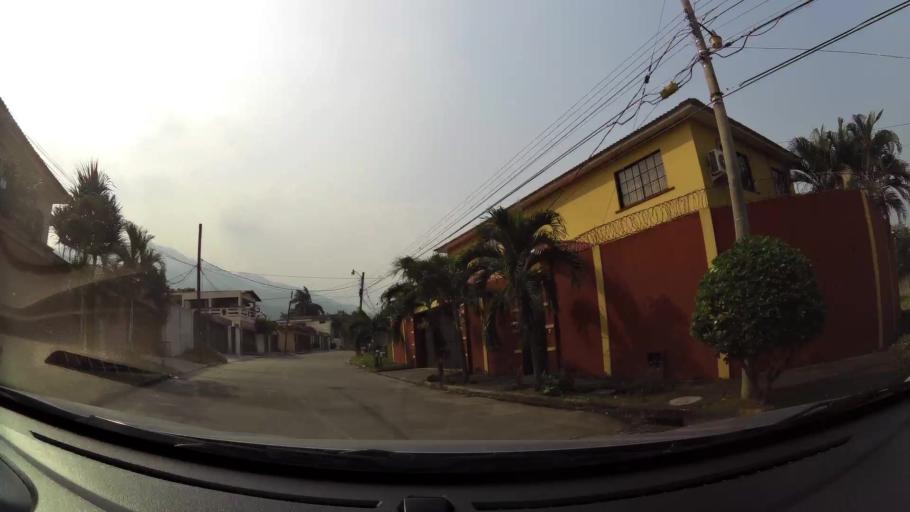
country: HN
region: Cortes
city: Armenta
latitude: 15.4924
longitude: -88.0431
